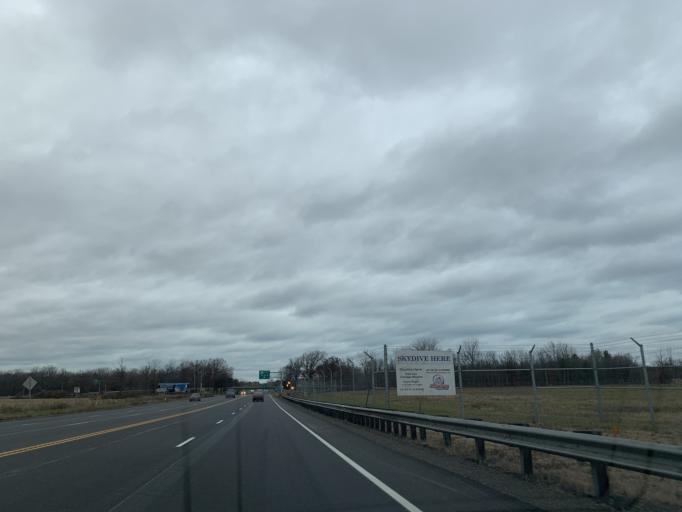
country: US
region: Indiana
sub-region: LaPorte County
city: Trail Creek
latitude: 41.6972
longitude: -86.8233
